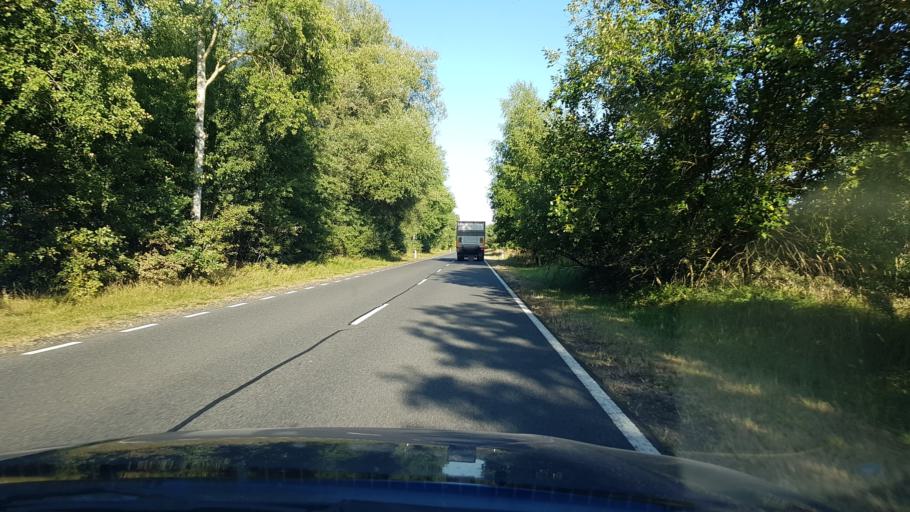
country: PL
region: West Pomeranian Voivodeship
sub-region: Powiat stargardzki
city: Marianowo
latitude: 53.4281
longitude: 15.2397
